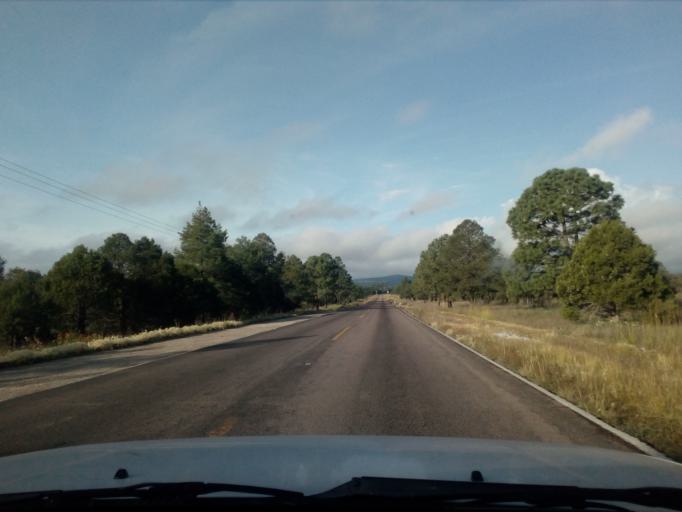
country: MX
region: Durango
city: Victoria de Durango
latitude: 23.9297
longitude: -104.9227
